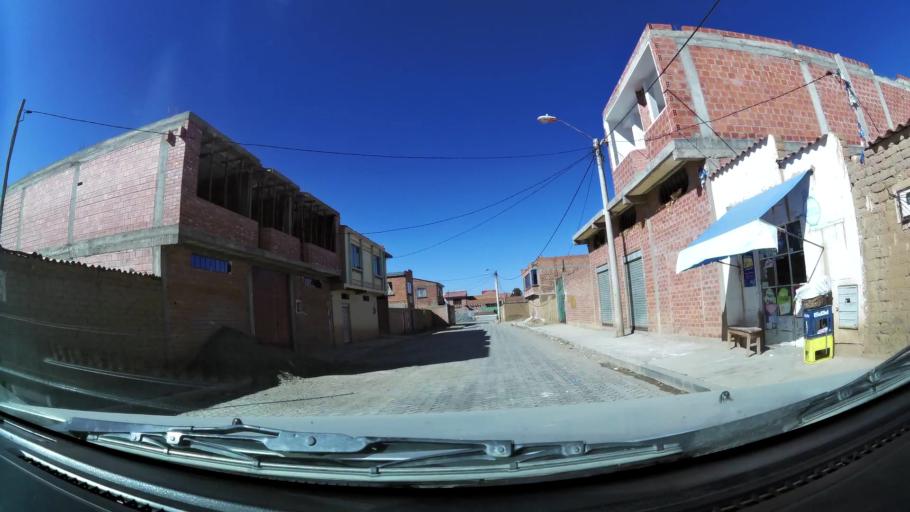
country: BO
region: La Paz
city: La Paz
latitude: -16.5344
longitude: -68.2259
